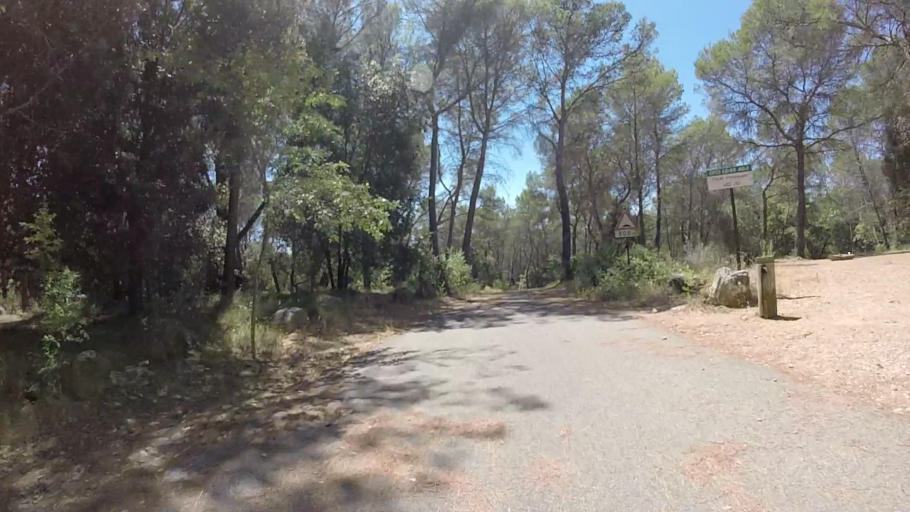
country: FR
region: Provence-Alpes-Cote d'Azur
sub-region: Departement des Alpes-Maritimes
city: Vallauris
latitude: 43.6118
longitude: 7.0438
